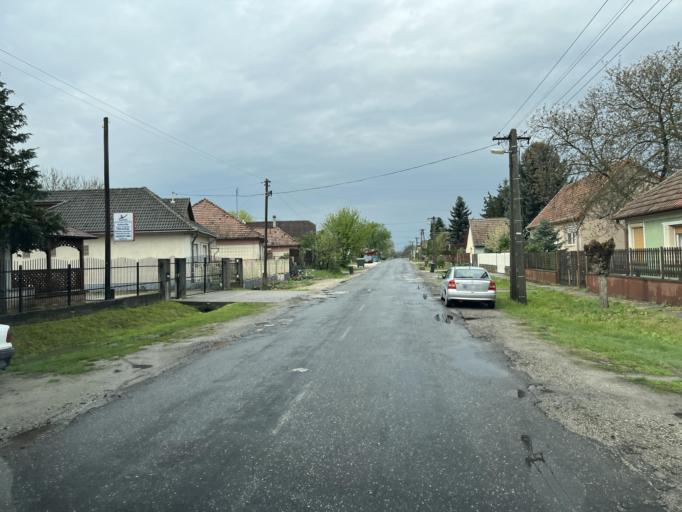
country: HU
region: Pest
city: Nyaregyhaza
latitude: 47.2530
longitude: 19.4941
